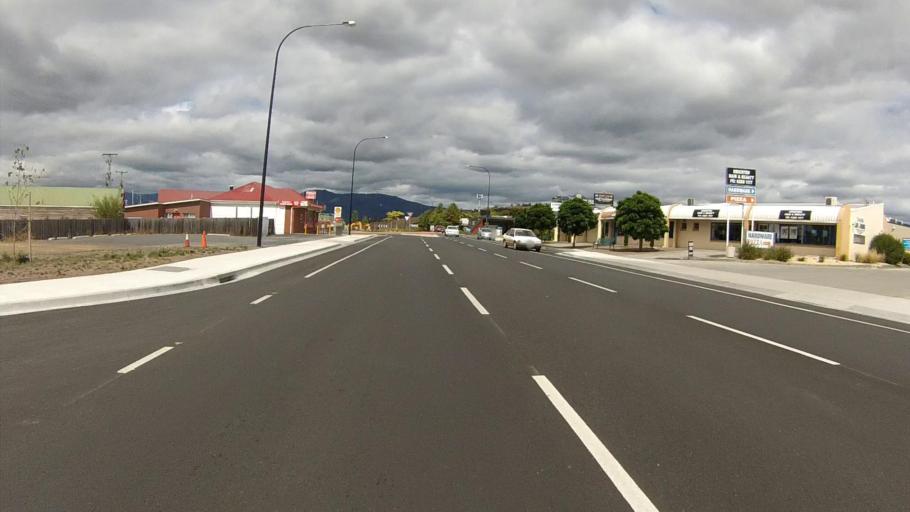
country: AU
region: Tasmania
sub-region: Brighton
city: Bridgewater
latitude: -42.6993
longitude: 147.2517
